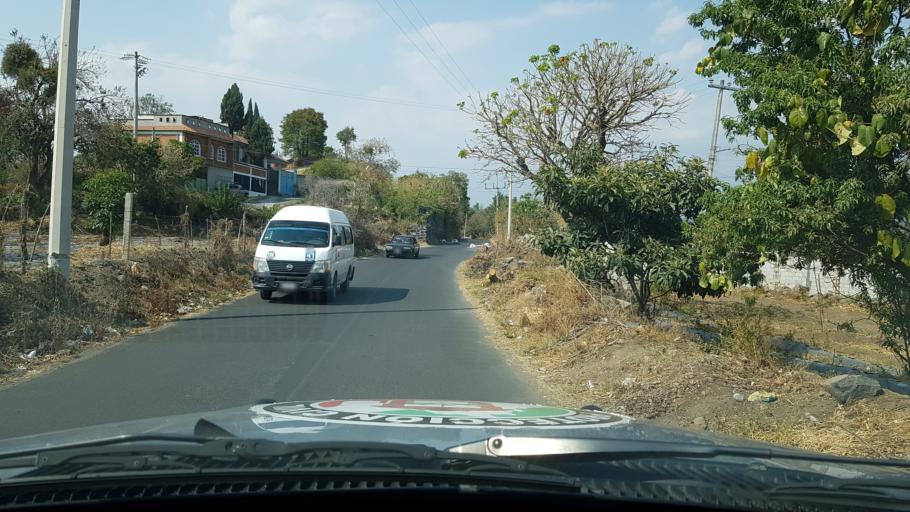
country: MX
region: Mexico
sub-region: Atlautla
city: San Andres Tlalamac
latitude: 18.9727
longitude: -98.8154
